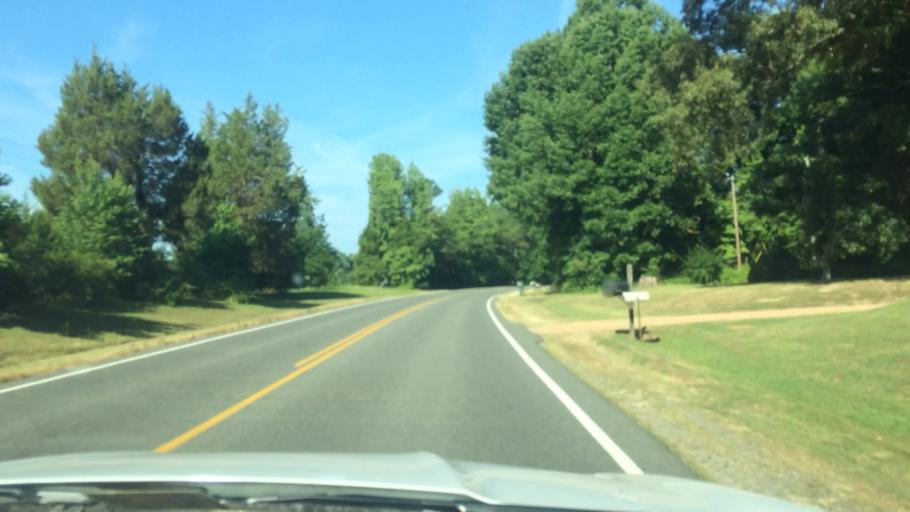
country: US
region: Virginia
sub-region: Northumberland County
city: Heathsville
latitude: 37.8496
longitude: -76.5967
